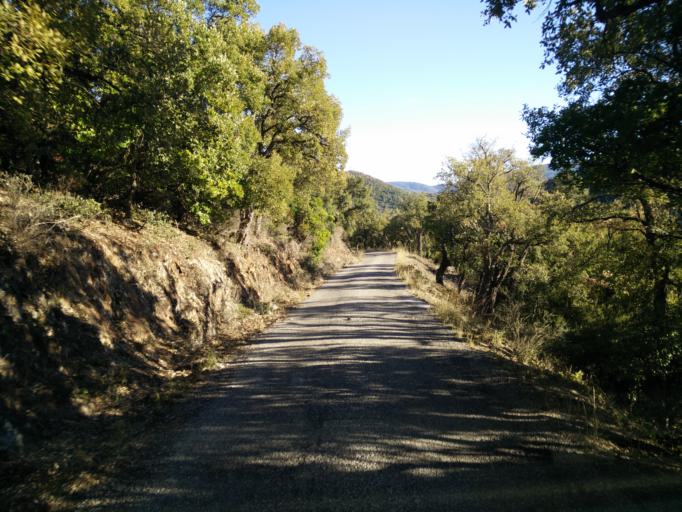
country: FR
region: Provence-Alpes-Cote d'Azur
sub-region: Departement du Var
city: Collobrieres
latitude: 43.2624
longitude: 6.2946
